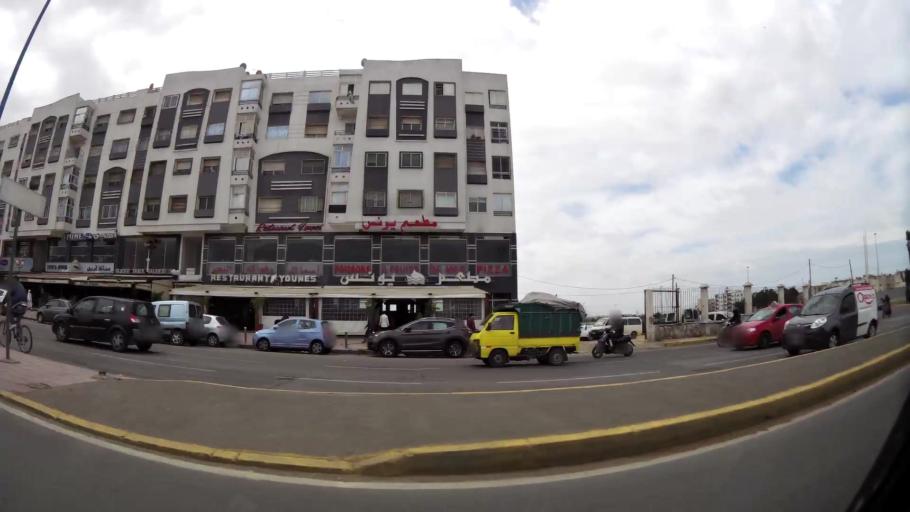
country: MA
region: Grand Casablanca
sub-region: Casablanca
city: Casablanca
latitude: 33.5728
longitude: -7.5629
